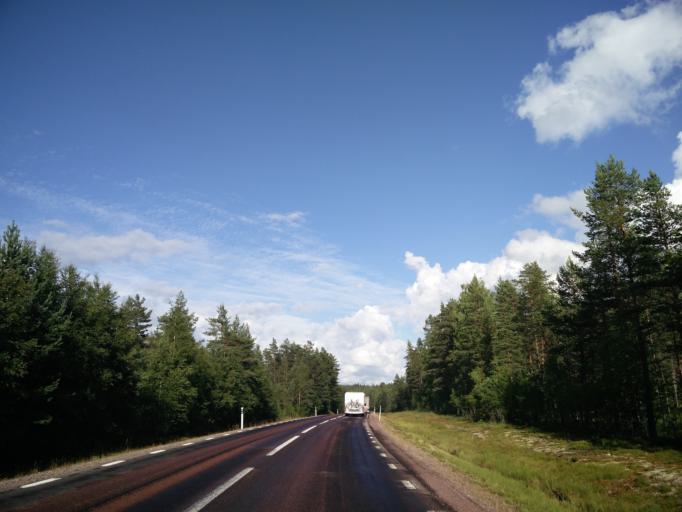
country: SE
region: Vaermland
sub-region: Hagfors Kommun
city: Ekshaerad
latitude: 60.4822
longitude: 13.3921
